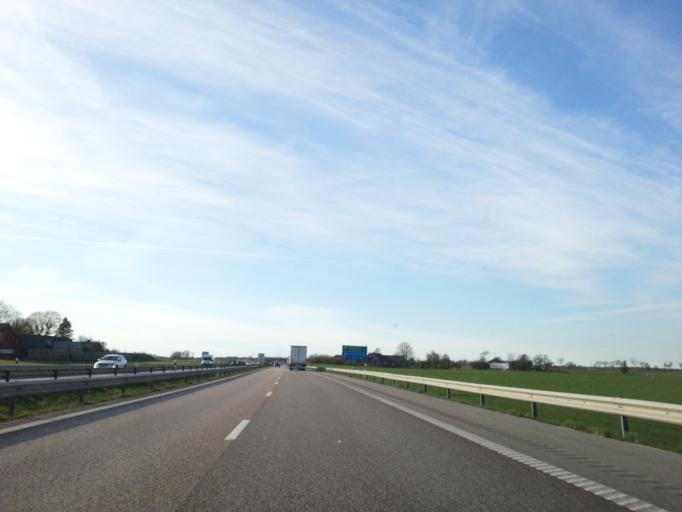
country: SE
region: Skane
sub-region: Helsingborg
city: Glumslov
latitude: 55.9602
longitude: 12.8008
